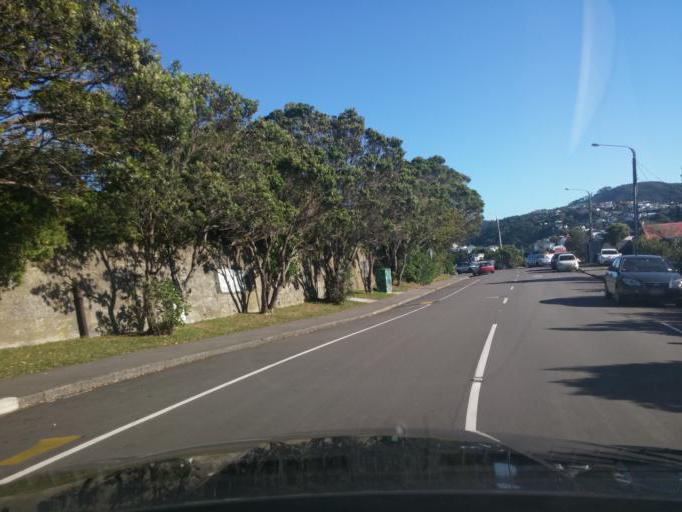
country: NZ
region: Wellington
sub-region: Wellington City
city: Kelburn
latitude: -41.2801
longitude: 174.7595
